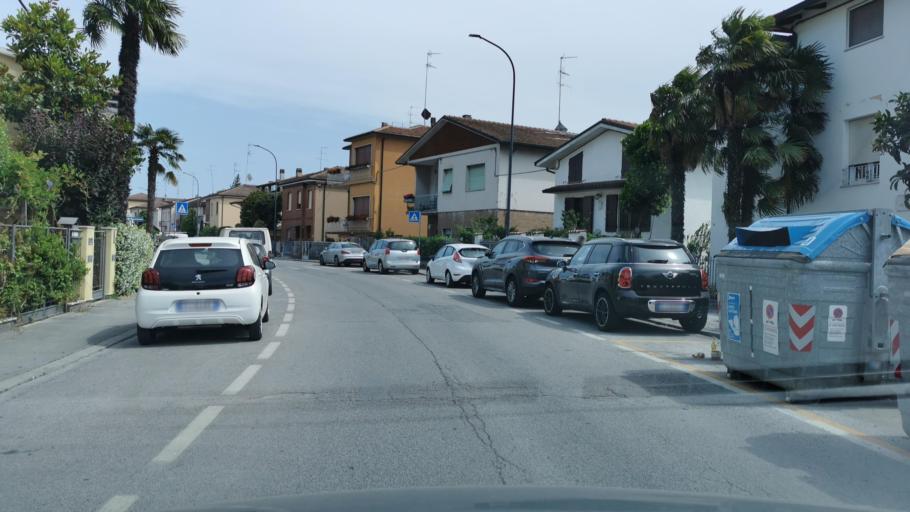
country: IT
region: Emilia-Romagna
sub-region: Provincia di Ravenna
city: Ravenna
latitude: 44.4172
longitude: 12.1823
